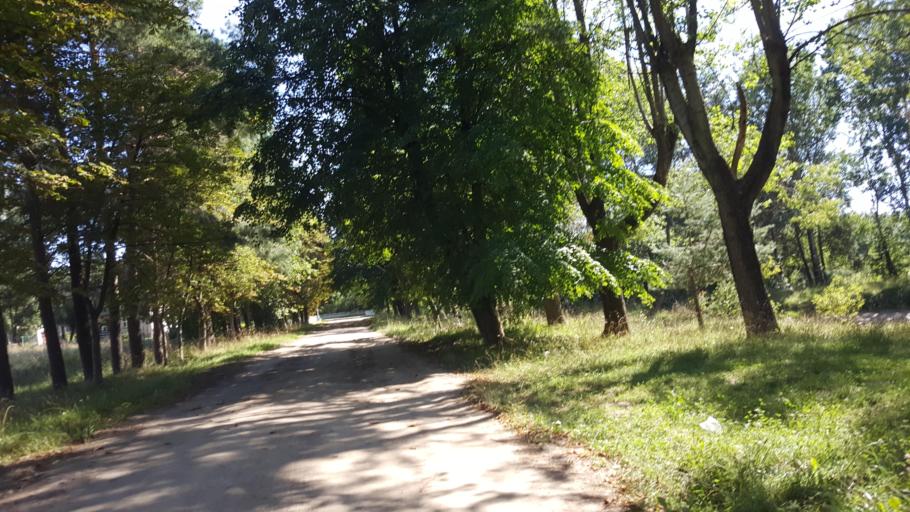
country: BY
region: Brest
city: Charnawchytsy
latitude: 52.2563
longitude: 23.5833
